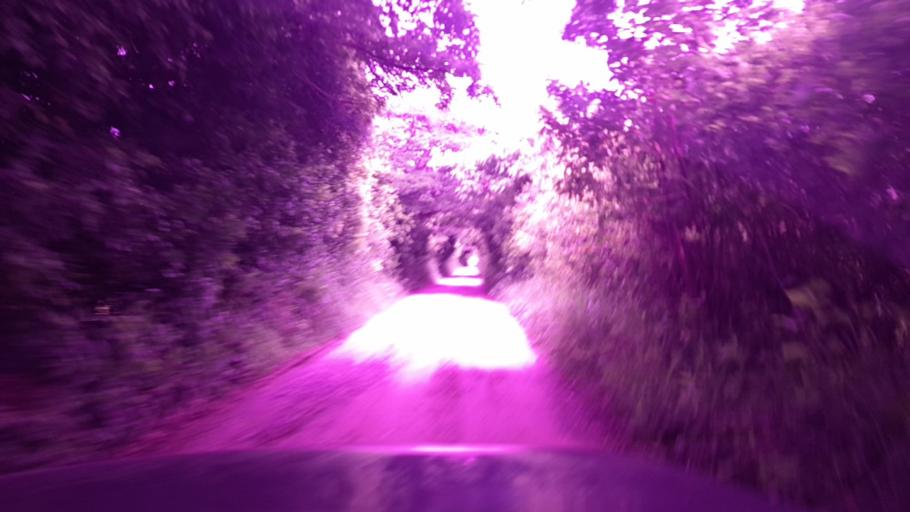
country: CO
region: Valle del Cauca
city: Bugalagrande
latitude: 4.1700
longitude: -76.0763
